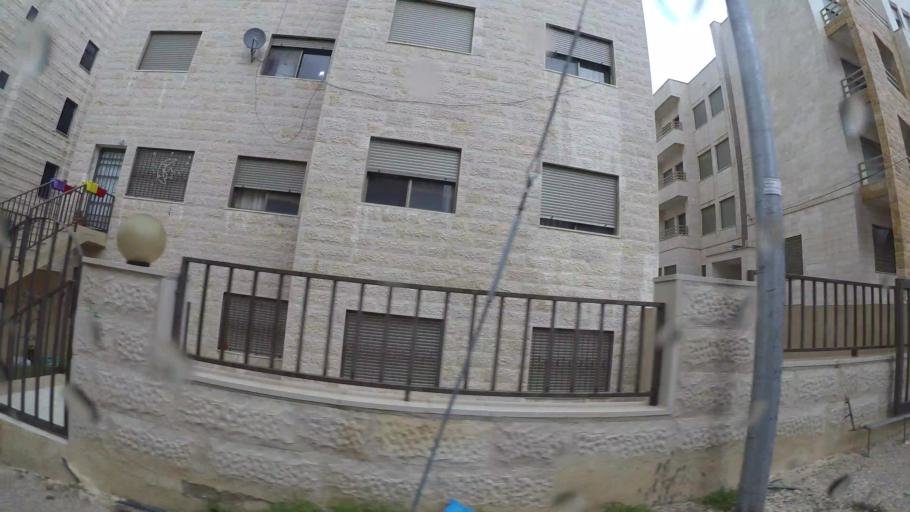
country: JO
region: Amman
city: Al Jubayhah
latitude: 32.0300
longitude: 35.8775
